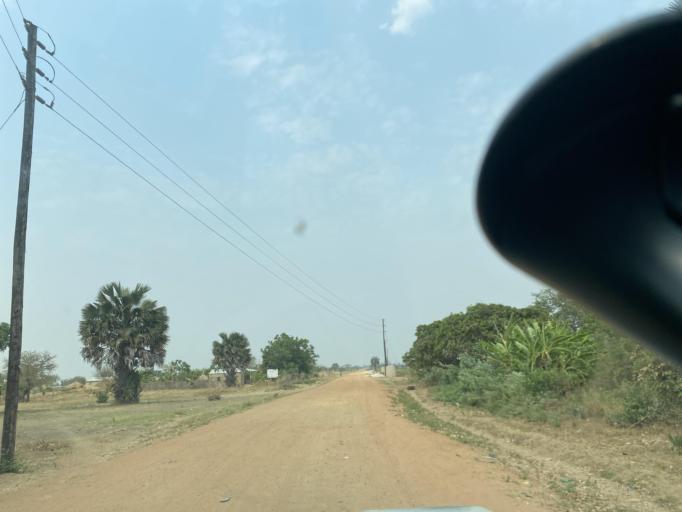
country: ZM
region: Lusaka
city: Kafue
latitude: -15.6722
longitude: 28.0179
